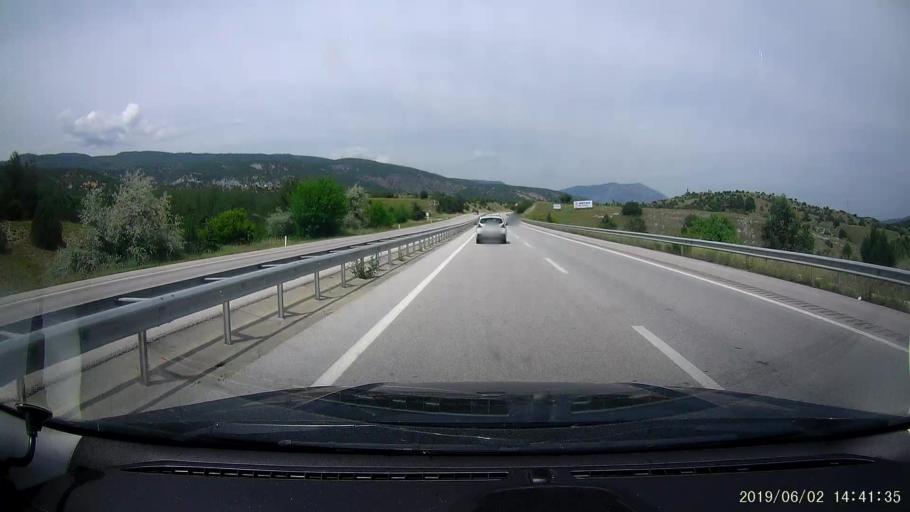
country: TR
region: Corum
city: Hacihamza
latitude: 41.0890
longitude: 34.3421
